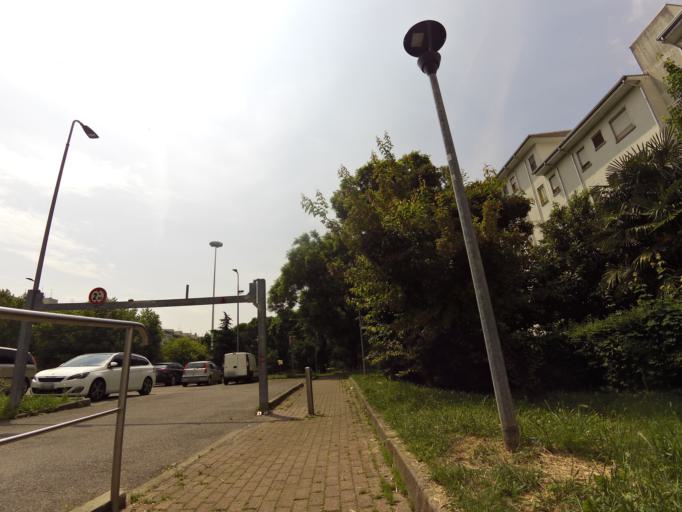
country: IT
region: Lombardy
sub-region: Citta metropolitana di Milano
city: Linate
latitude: 45.4419
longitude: 9.2628
